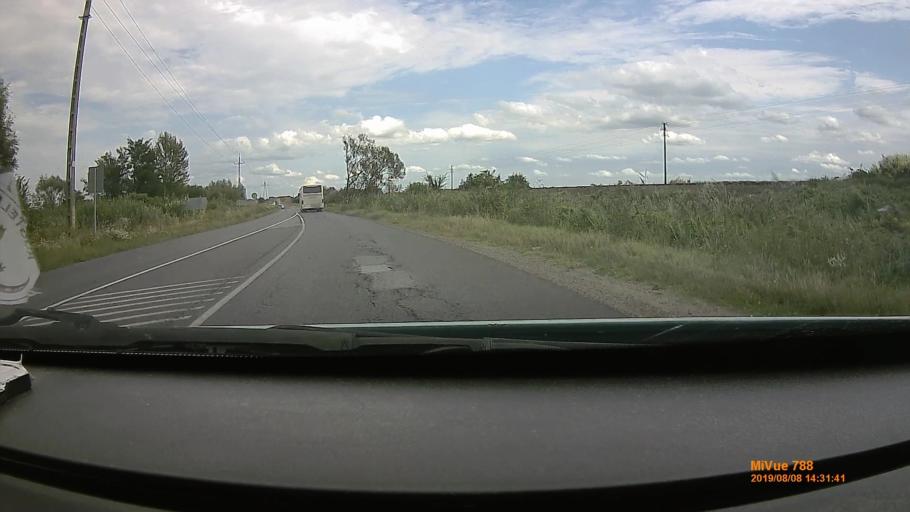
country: HU
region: Szabolcs-Szatmar-Bereg
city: Mateszalka
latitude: 47.9403
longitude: 22.3293
